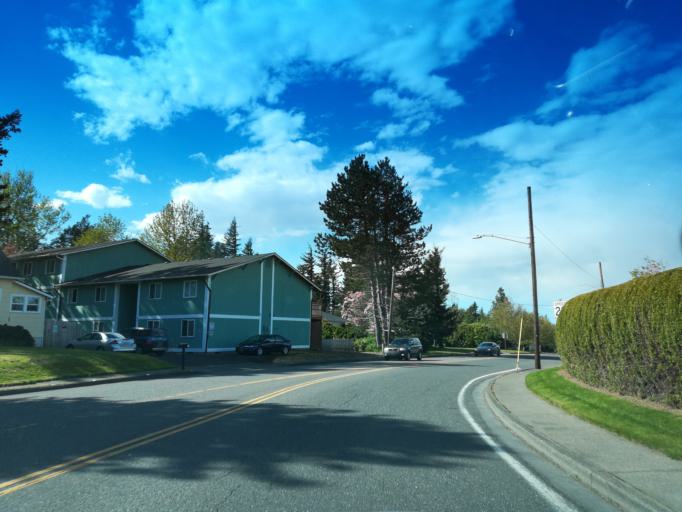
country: US
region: Oregon
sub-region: Multnomah County
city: Troutdale
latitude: 45.5338
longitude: -122.3883
